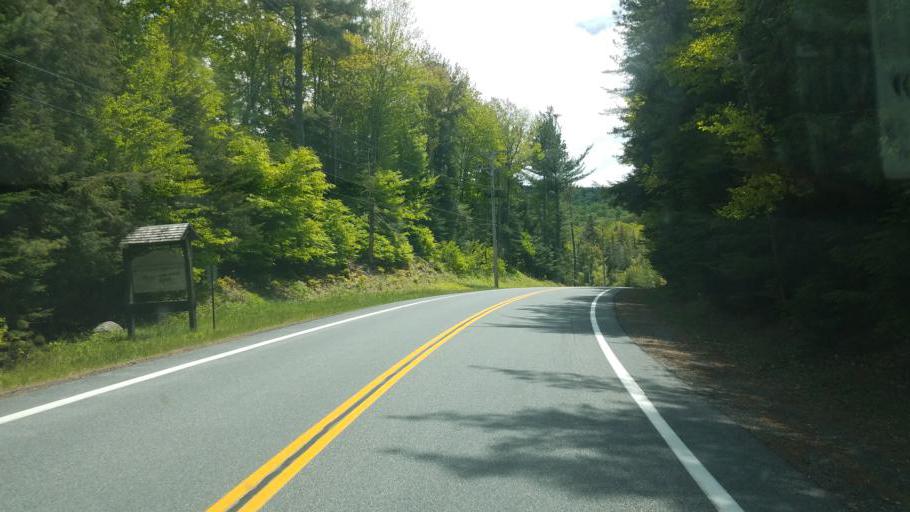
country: US
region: New York
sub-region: Hamilton County
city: Lake Pleasant
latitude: 43.8067
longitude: -74.6091
